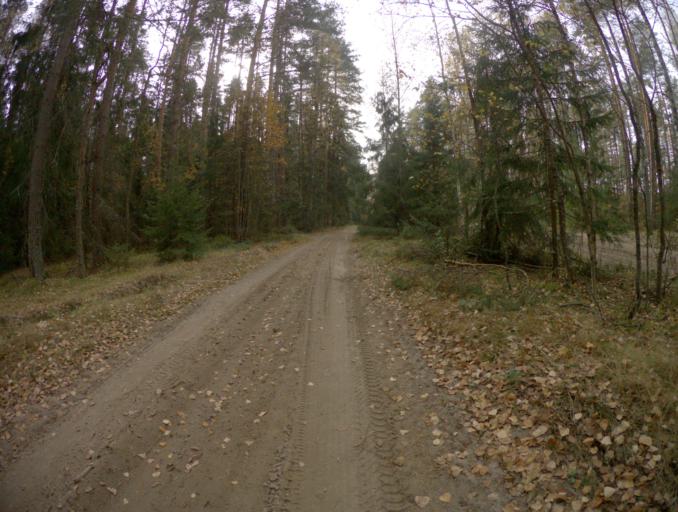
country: RU
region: Vladimir
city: Vorsha
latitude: 55.9642
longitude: 40.1489
